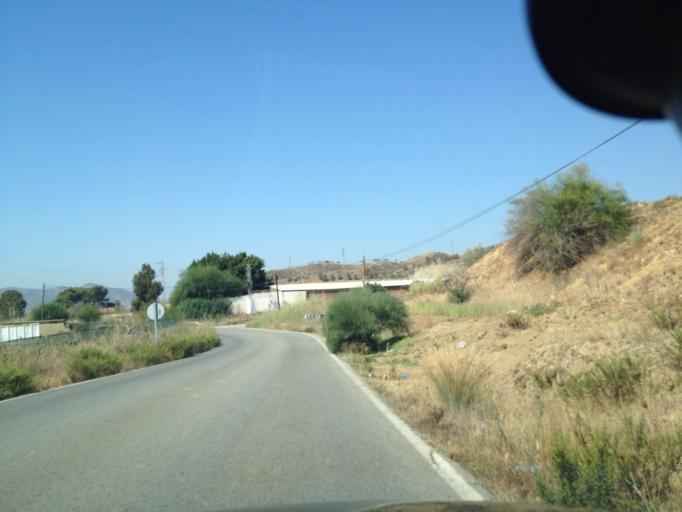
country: ES
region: Andalusia
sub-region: Provincia de Malaga
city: Alhaurin de la Torre
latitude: 36.7197
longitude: -4.5173
